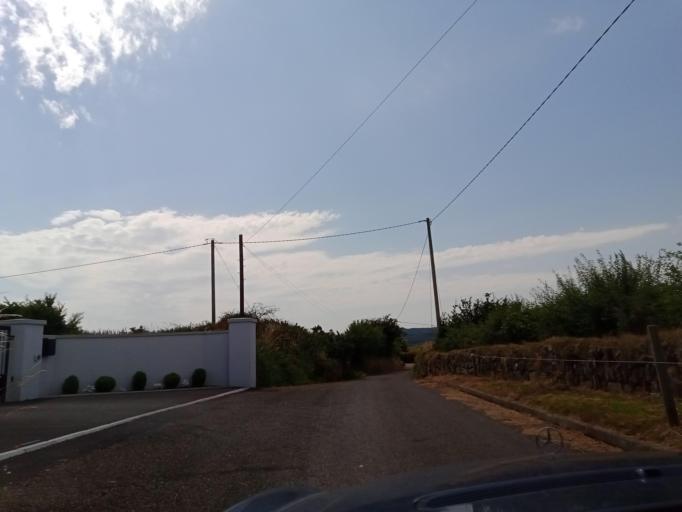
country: IE
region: Leinster
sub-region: Kilkenny
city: Mooncoin
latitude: 52.2664
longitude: -7.2294
